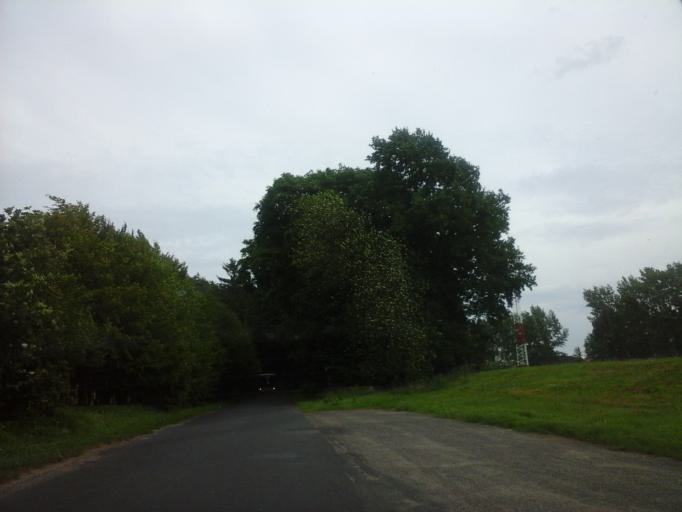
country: PL
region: West Pomeranian Voivodeship
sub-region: Powiat stargardzki
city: Marianowo
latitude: 53.3366
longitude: 15.1977
